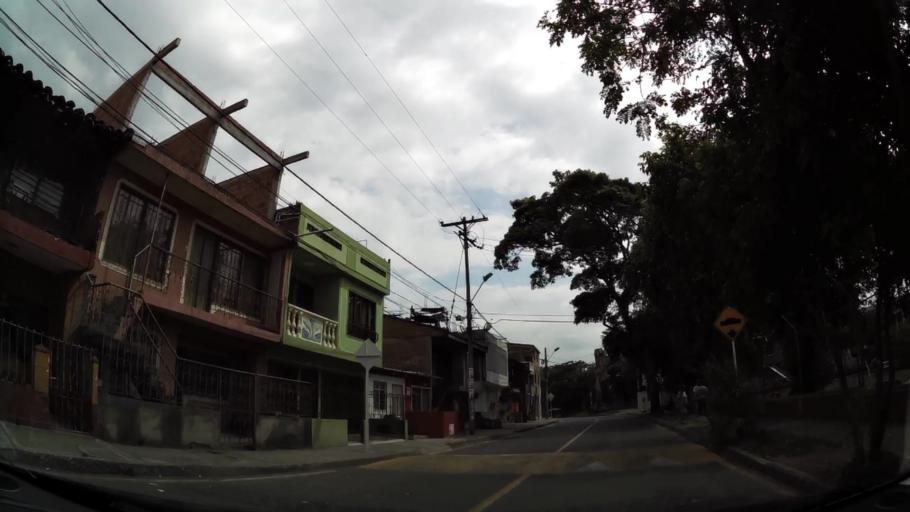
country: CO
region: Valle del Cauca
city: Cali
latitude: 3.4957
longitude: -76.4875
